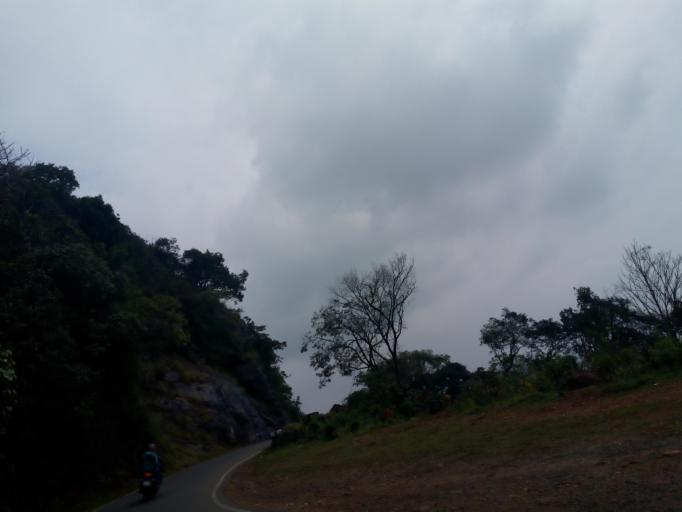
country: IN
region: Karnataka
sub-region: Dakshina Kannada
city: Sulya
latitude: 12.3815
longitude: 75.5157
